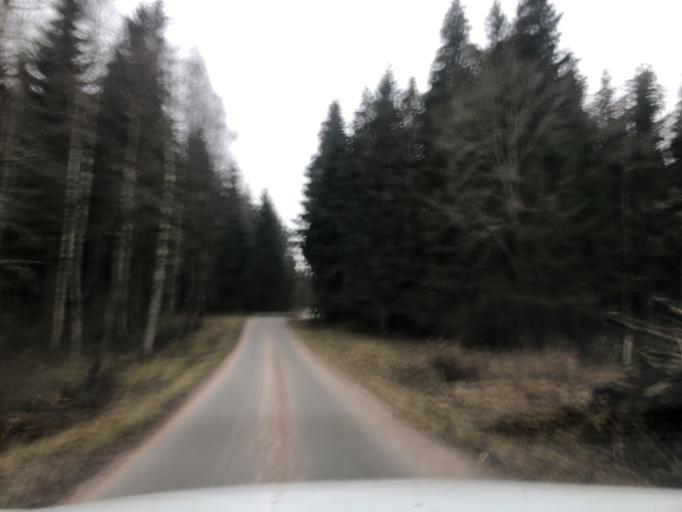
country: SE
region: Vaestra Goetaland
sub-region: Ulricehamns Kommun
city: Ulricehamn
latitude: 57.8757
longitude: 13.5631
